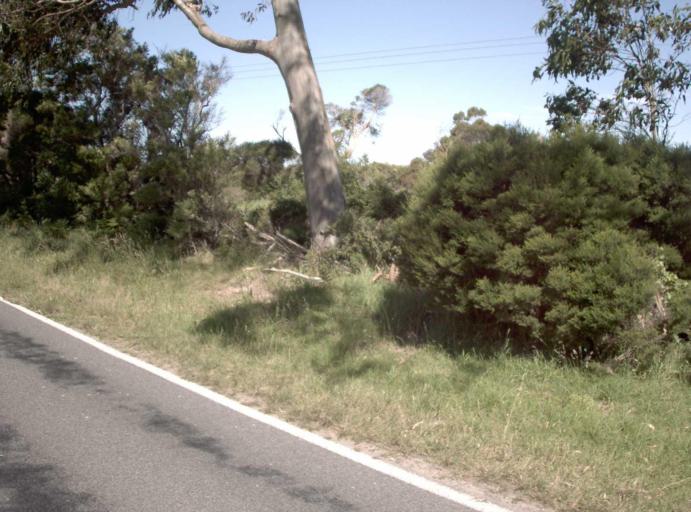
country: AU
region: Victoria
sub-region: Latrobe
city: Morwell
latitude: -38.6645
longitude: 146.3606
